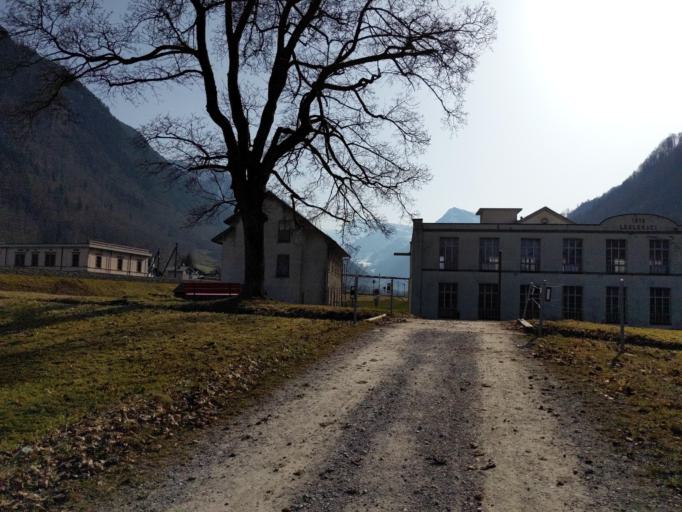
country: CH
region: Glarus
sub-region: Glarus
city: Luchsingen
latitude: 46.9516
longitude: 9.0292
